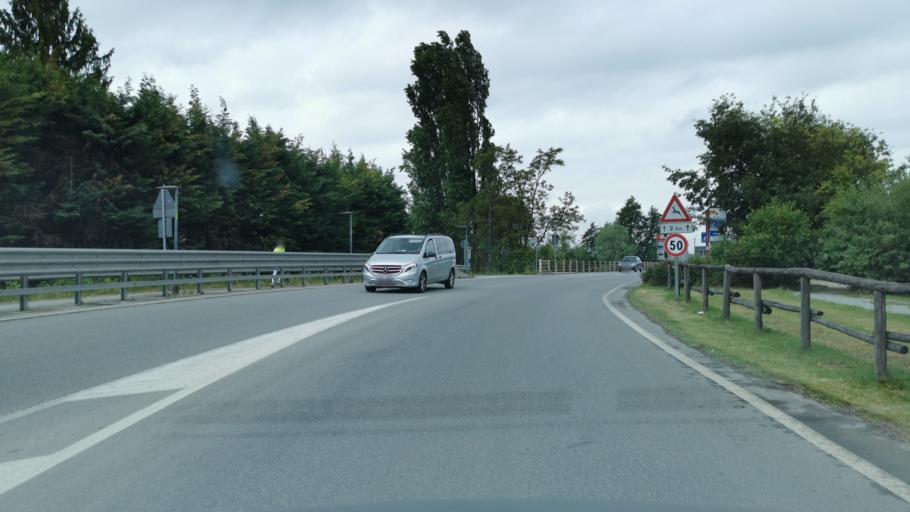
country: IT
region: Piedmont
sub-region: Provincia di Cuneo
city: Savigliano
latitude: 44.6408
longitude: 7.6500
